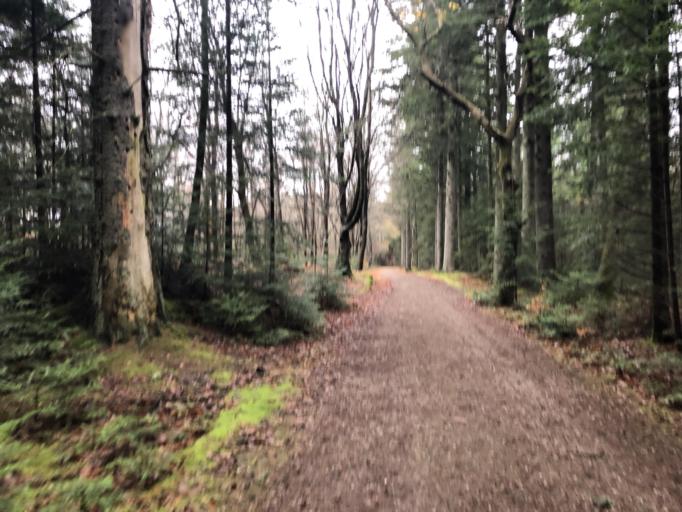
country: DK
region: Central Jutland
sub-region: Holstebro Kommune
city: Ulfborg
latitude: 56.2882
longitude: 8.1677
